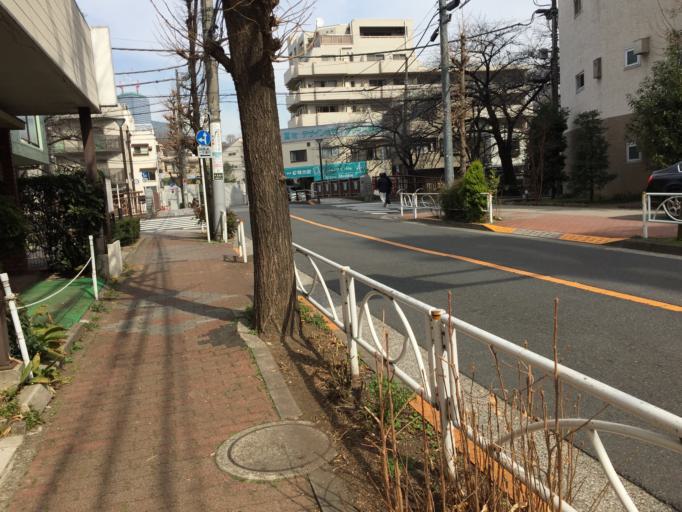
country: JP
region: Tokyo
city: Tokyo
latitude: 35.6482
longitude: 139.6941
